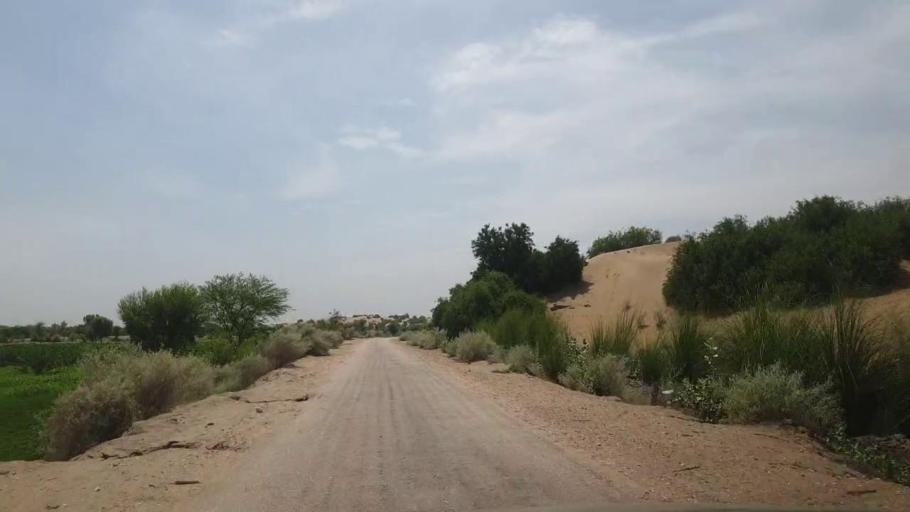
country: PK
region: Sindh
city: Kot Diji
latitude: 27.1054
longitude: 69.0774
